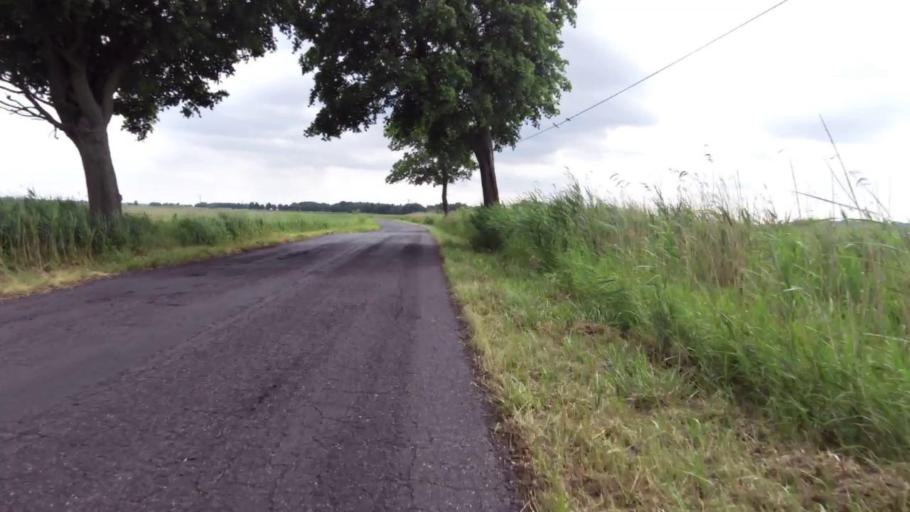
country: PL
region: West Pomeranian Voivodeship
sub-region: Powiat goleniowski
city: Stepnica
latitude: 53.6850
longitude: 14.5495
